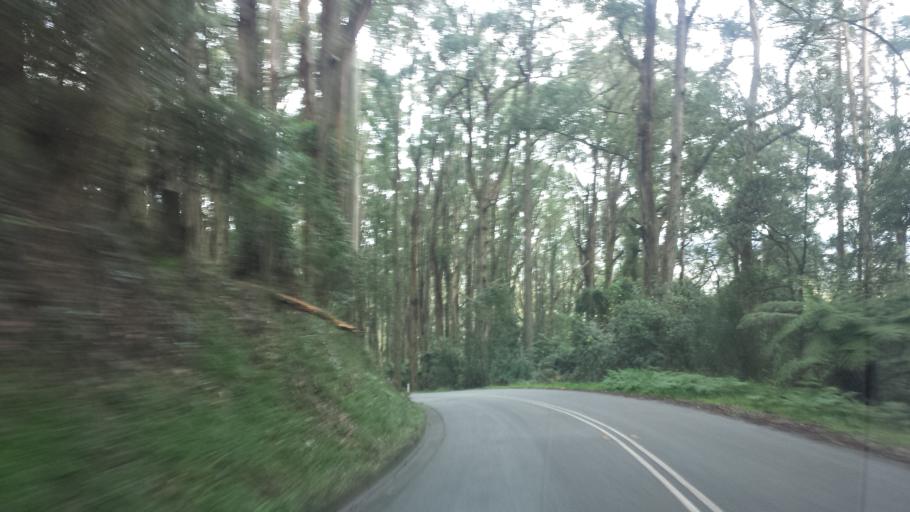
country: AU
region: Victoria
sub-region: Yarra Ranges
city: Belgrave
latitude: -37.8895
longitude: 145.3457
